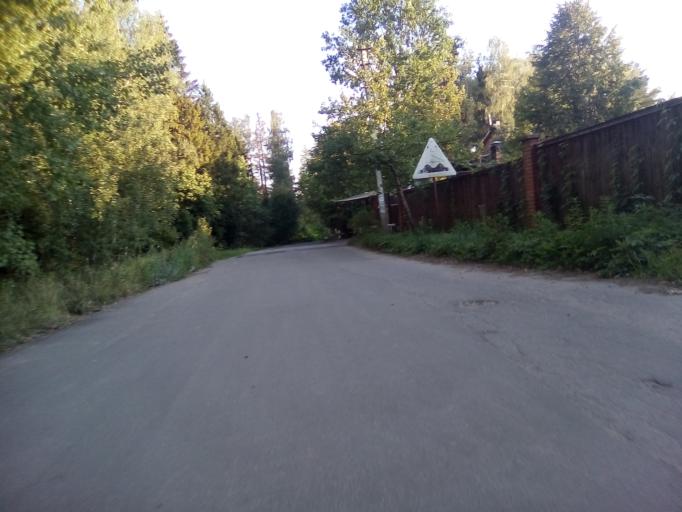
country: RU
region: Moskovskaya
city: Krasnoznamensk
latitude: 55.5781
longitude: 37.0430
